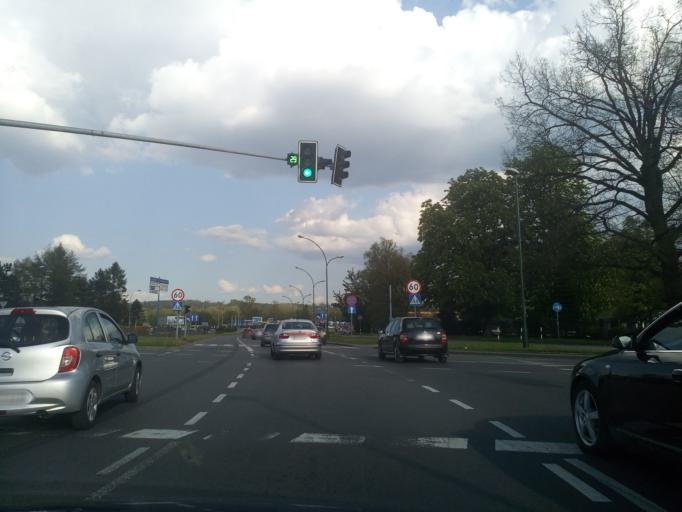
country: PL
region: Lesser Poland Voivodeship
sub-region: Powiat nowosadecki
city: Nowy Sacz
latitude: 49.6174
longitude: 20.7146
